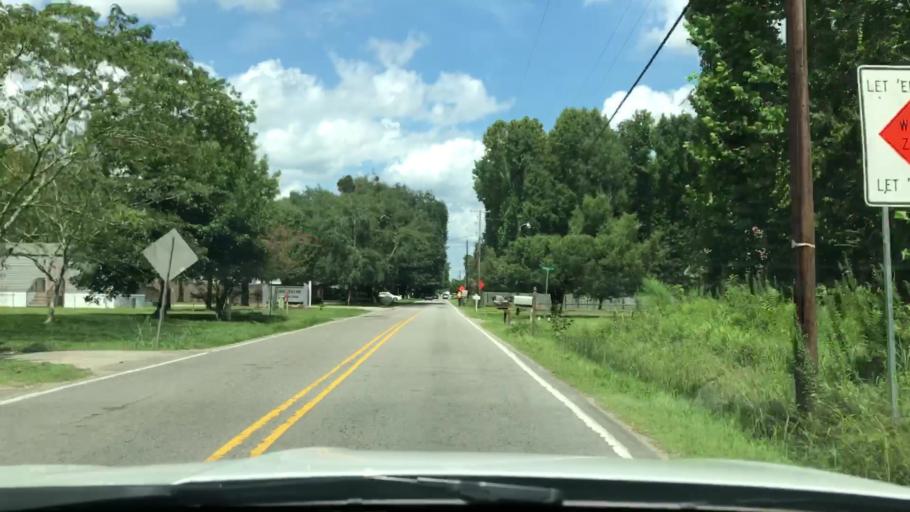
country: US
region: South Carolina
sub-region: Dorchester County
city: Summerville
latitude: 33.0352
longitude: -80.1879
